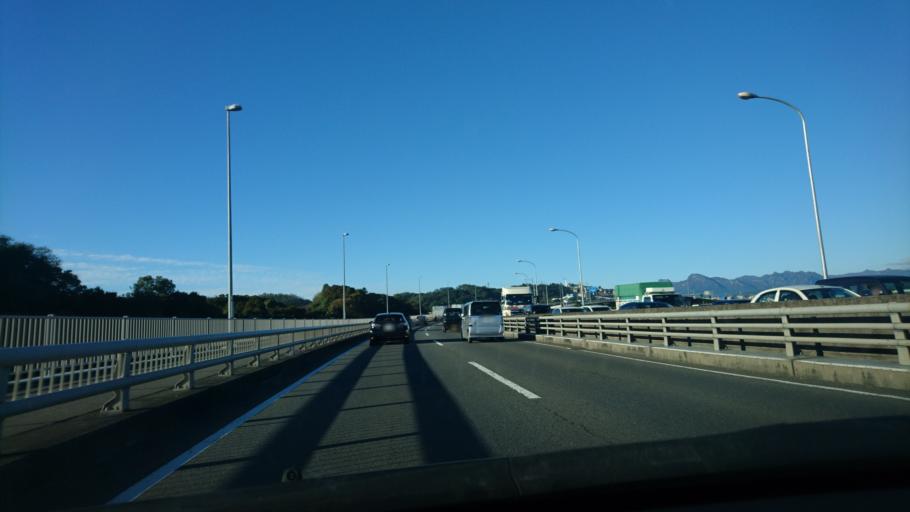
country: JP
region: Gunma
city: Annaka
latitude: 36.3345
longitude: 138.9366
